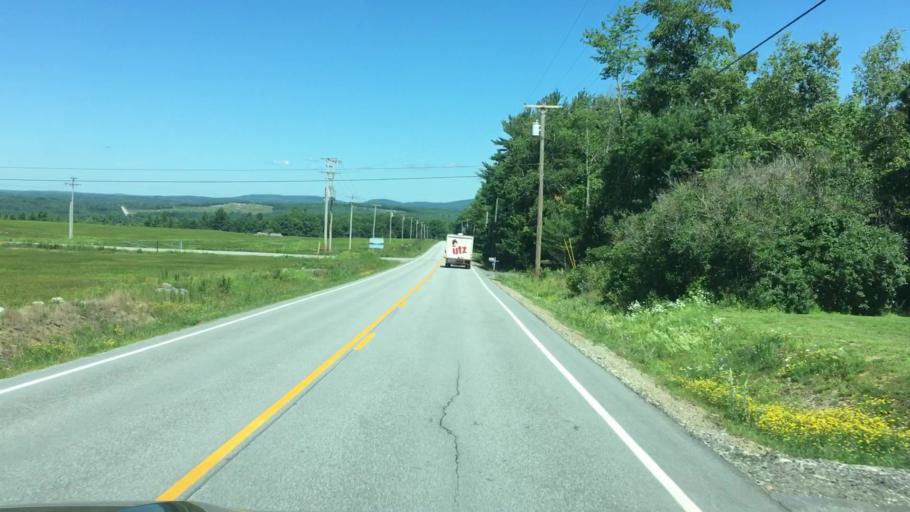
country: US
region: Maine
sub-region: Hancock County
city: Orland
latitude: 44.5486
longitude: -68.6902
